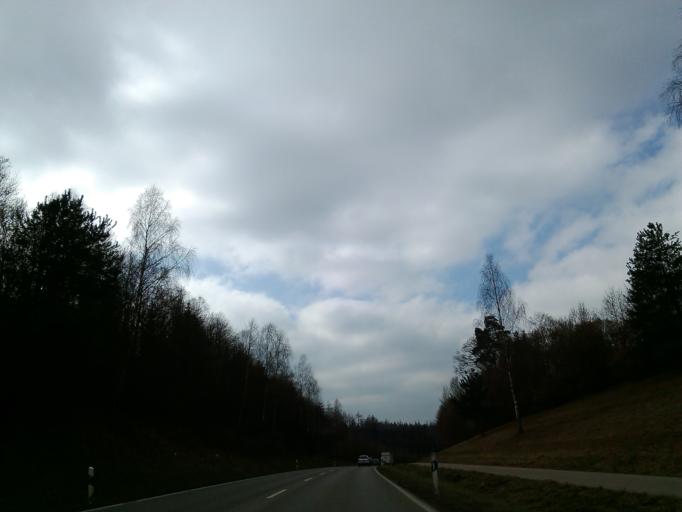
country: DE
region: Bavaria
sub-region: Swabia
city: Ursberg
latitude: 48.2555
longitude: 10.4296
